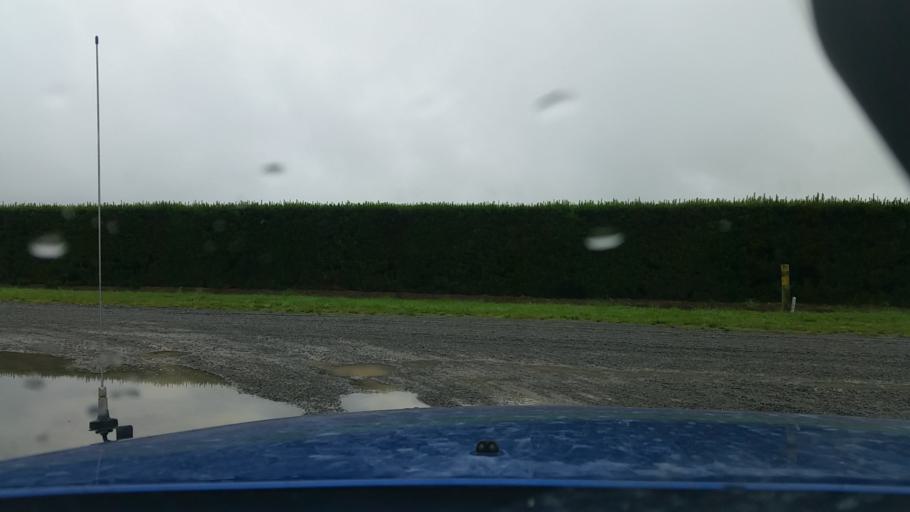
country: NZ
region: Canterbury
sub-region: Ashburton District
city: Methven
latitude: -43.6802
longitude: 171.6825
